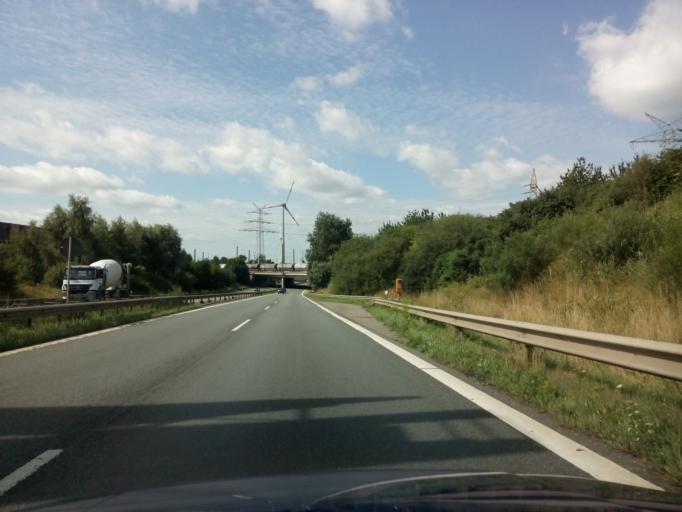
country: DE
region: Lower Saxony
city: Ritterhude
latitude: 53.1401
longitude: 8.7182
